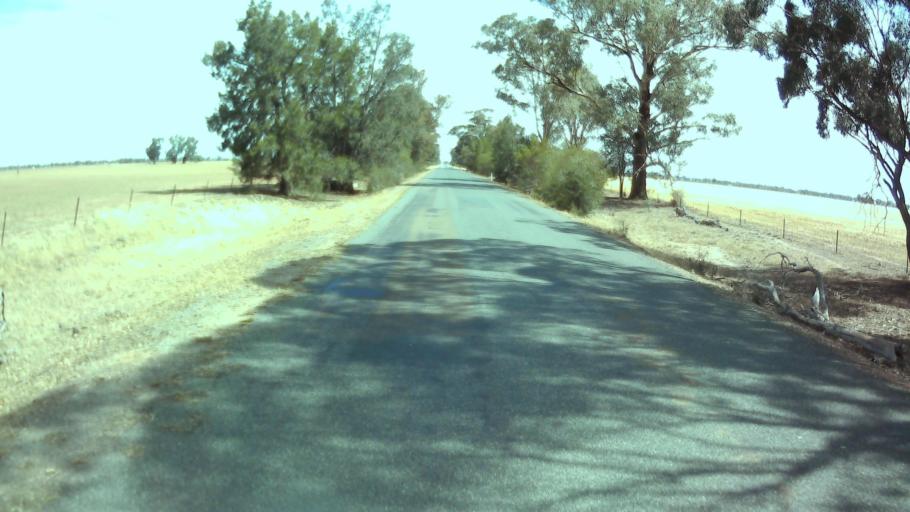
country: AU
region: New South Wales
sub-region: Weddin
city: Grenfell
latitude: -33.9740
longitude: 147.7793
